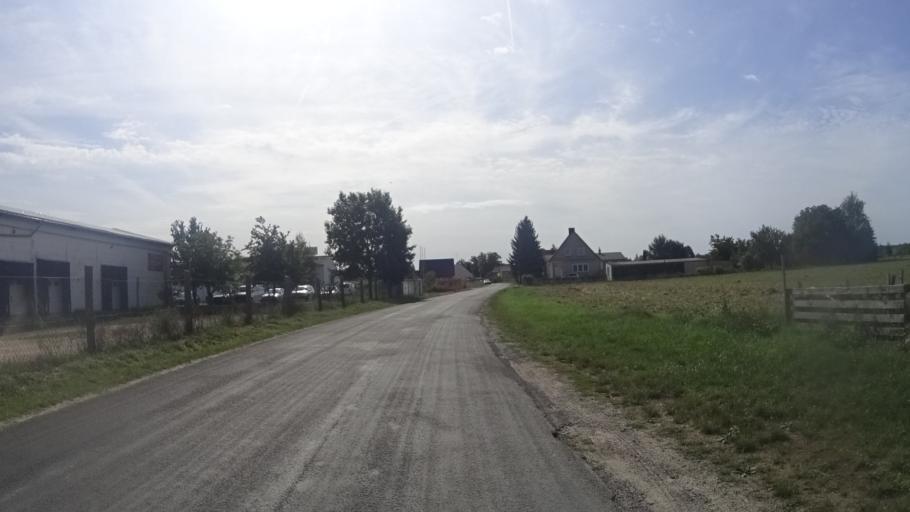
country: DE
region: Brandenburg
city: Golzow
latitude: 52.3105
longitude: 12.6956
